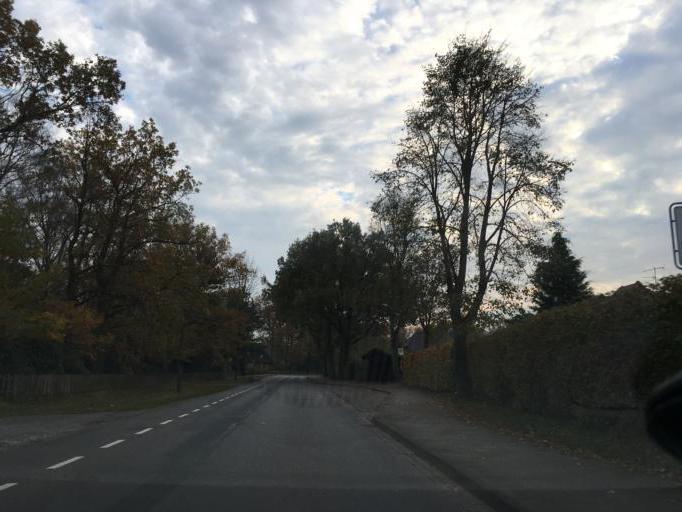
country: DE
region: Lower Saxony
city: Wietzendorf
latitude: 52.9243
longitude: 9.9792
